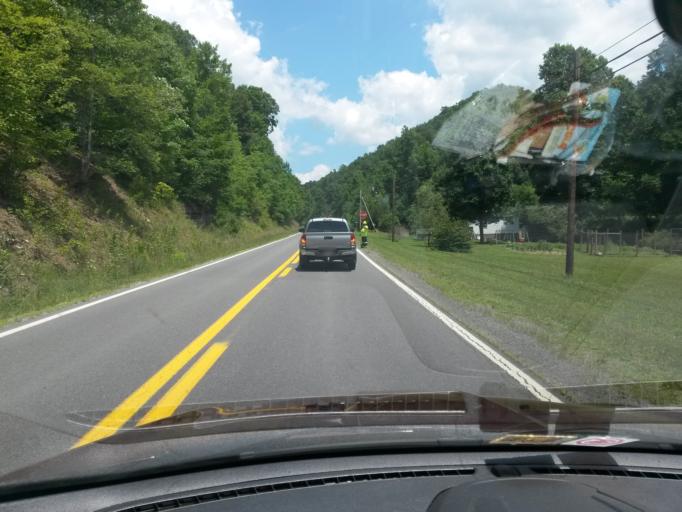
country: US
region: West Virginia
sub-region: Raleigh County
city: Sophia
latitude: 37.7028
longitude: -81.3297
